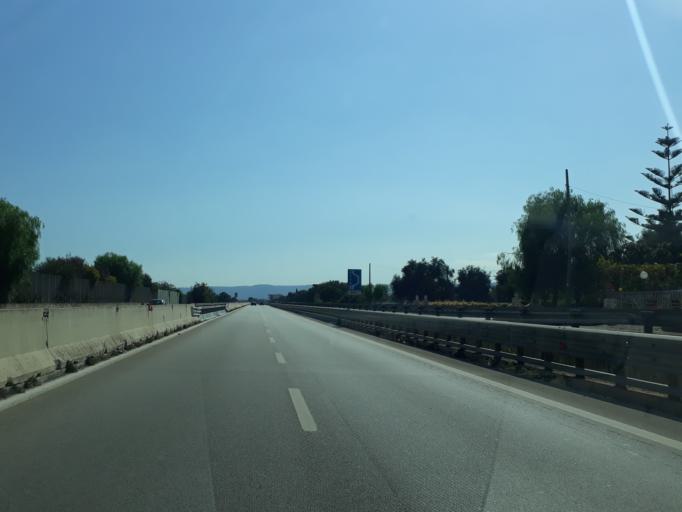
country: IT
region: Apulia
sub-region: Provincia di Brindisi
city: Fasano
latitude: 40.8679
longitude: 17.3447
